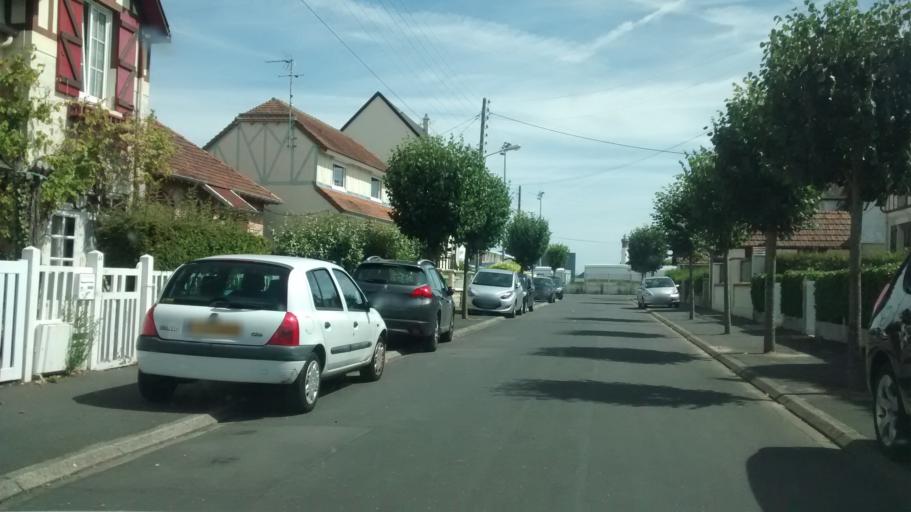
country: FR
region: Lower Normandy
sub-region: Departement du Calvados
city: Ouistreham
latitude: 49.2832
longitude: -0.2547
